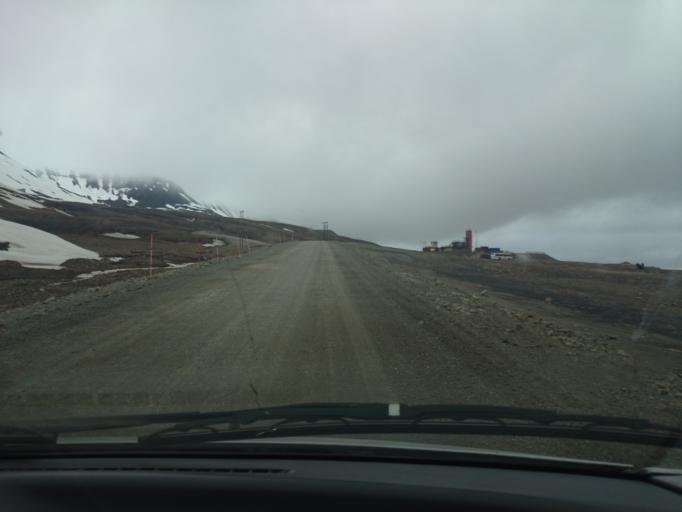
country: SJ
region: Svalbard
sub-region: Spitsbergen
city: Longyearbyen
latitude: 78.2385
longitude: 15.5226
